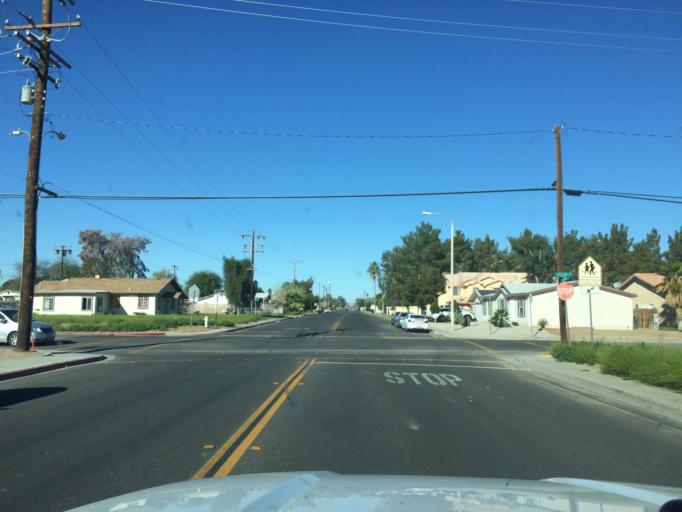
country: US
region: California
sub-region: Riverside County
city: Blythe
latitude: 33.6142
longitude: -114.5900
